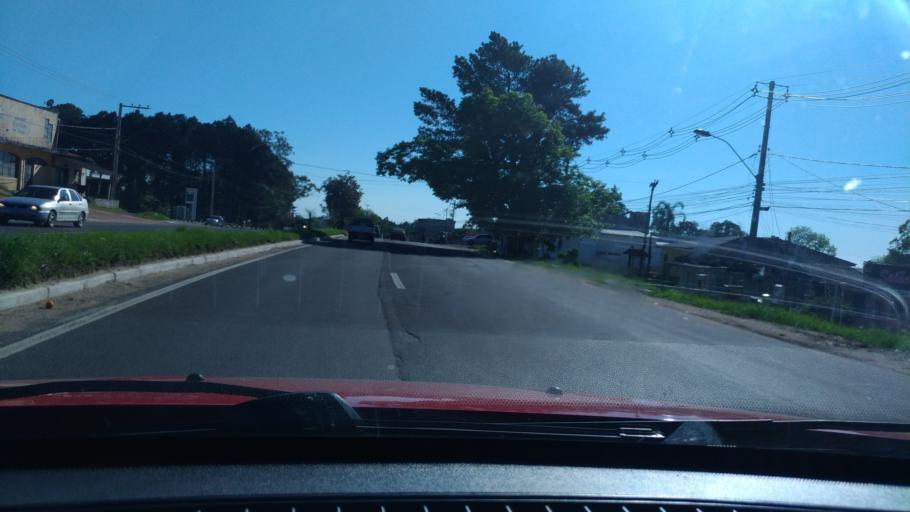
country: BR
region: Rio Grande do Sul
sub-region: Viamao
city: Viamao
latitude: -30.0903
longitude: -51.0625
